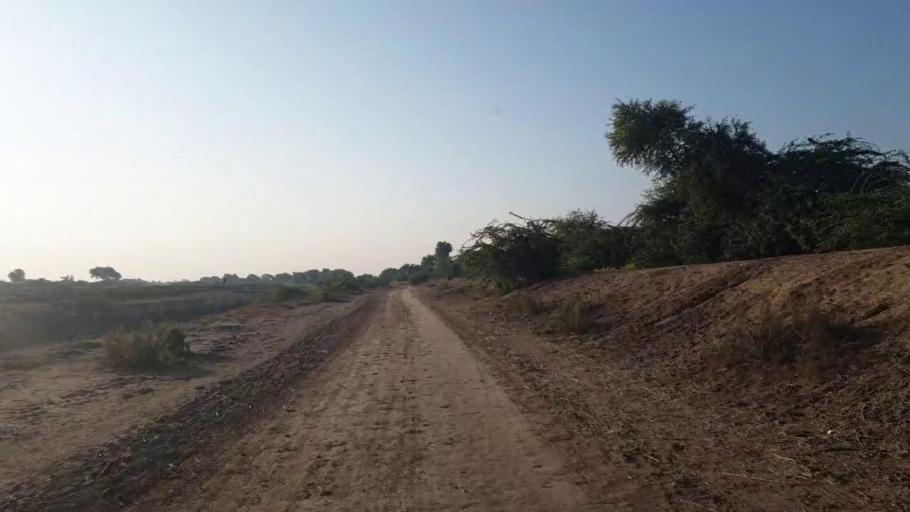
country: PK
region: Sindh
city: Badin
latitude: 24.6399
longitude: 68.7915
